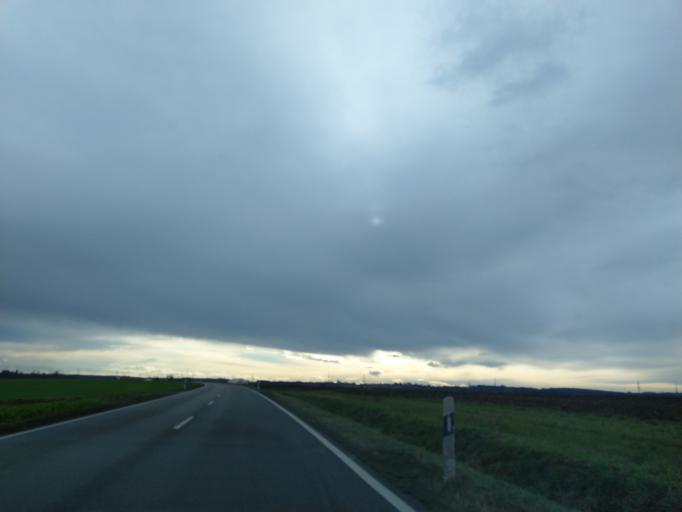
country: DE
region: Bavaria
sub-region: Lower Bavaria
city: Osterhofen
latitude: 48.6734
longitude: 13.0332
